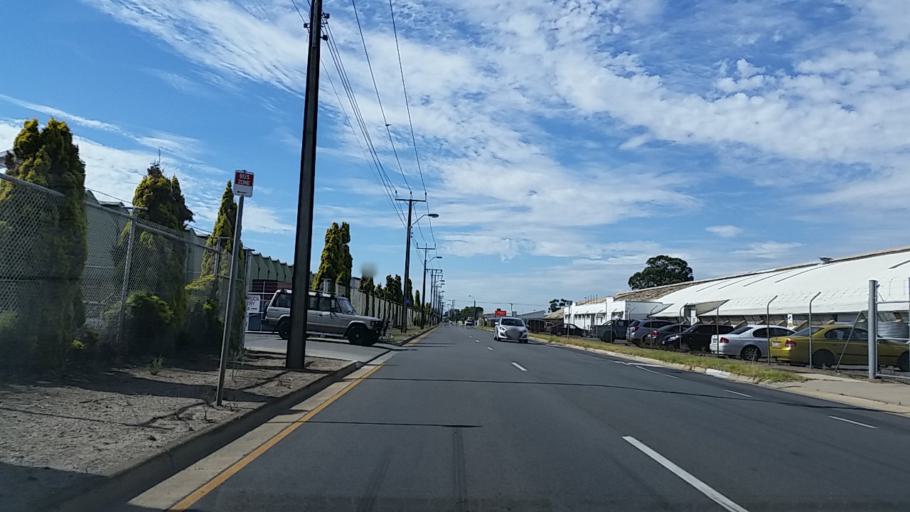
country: AU
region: South Australia
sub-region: Charles Sturt
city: Woodville North
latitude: -34.8584
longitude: 138.5384
